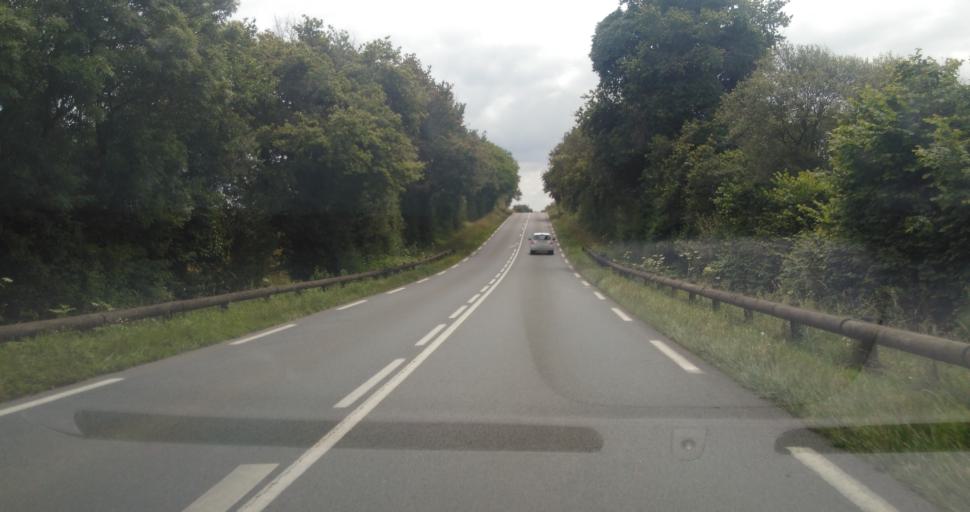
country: FR
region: Pays de la Loire
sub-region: Departement de la Vendee
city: Bournezeau
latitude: 46.6137
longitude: -1.1474
